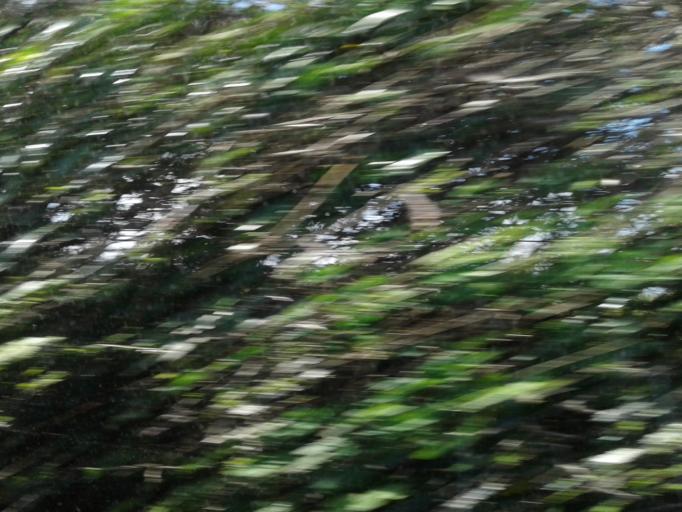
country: IE
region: Leinster
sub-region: Fingal County
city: Swords
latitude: 53.4853
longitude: -6.2899
